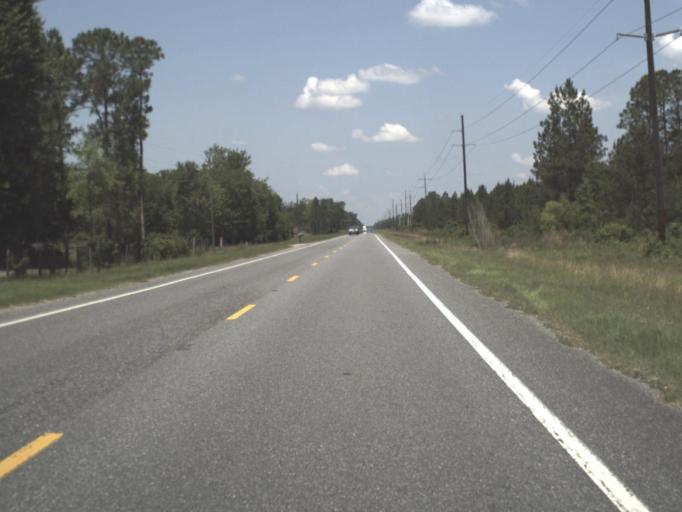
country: US
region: Florida
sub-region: Bradford County
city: Starke
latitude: 29.9674
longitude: -82.1990
